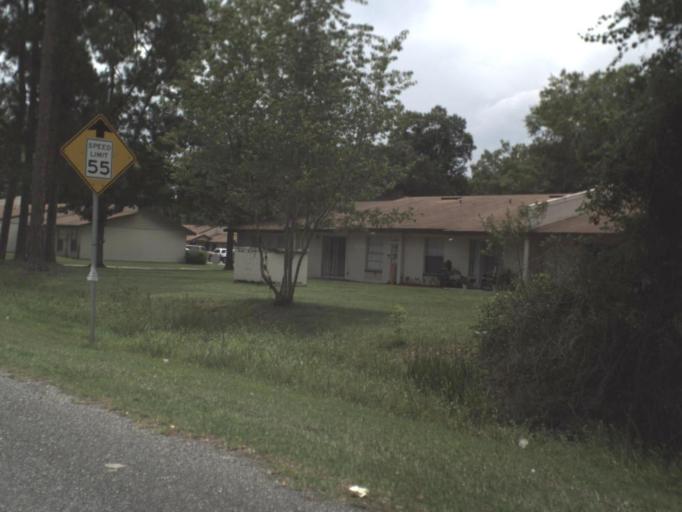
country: US
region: Florida
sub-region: Bradford County
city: Starke
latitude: 29.9446
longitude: -82.1325
